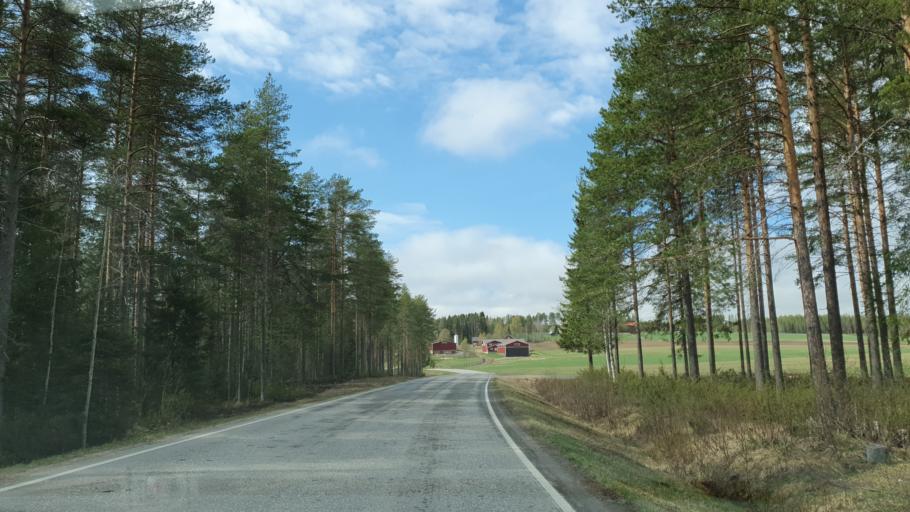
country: FI
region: Kainuu
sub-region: Kehys-Kainuu
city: Kuhmo
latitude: 64.1233
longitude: 29.6557
